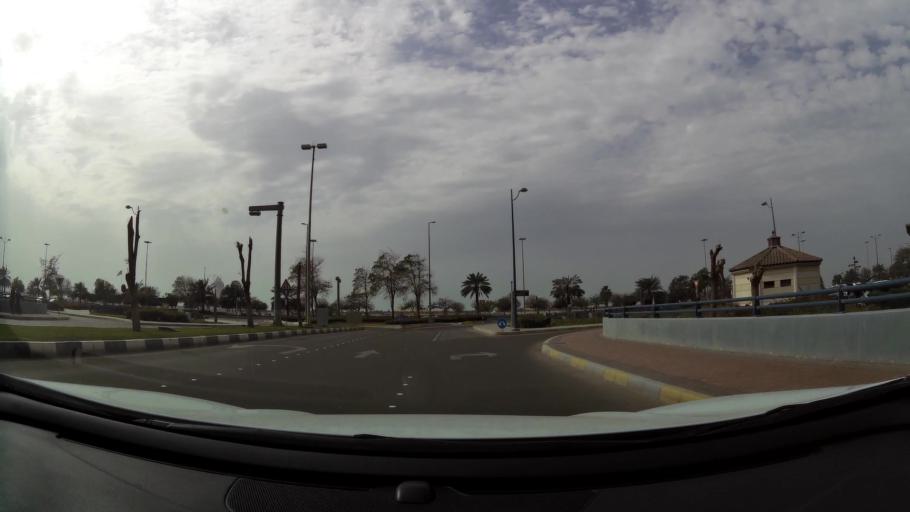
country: AE
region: Abu Dhabi
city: Abu Dhabi
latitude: 24.4818
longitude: 54.3482
